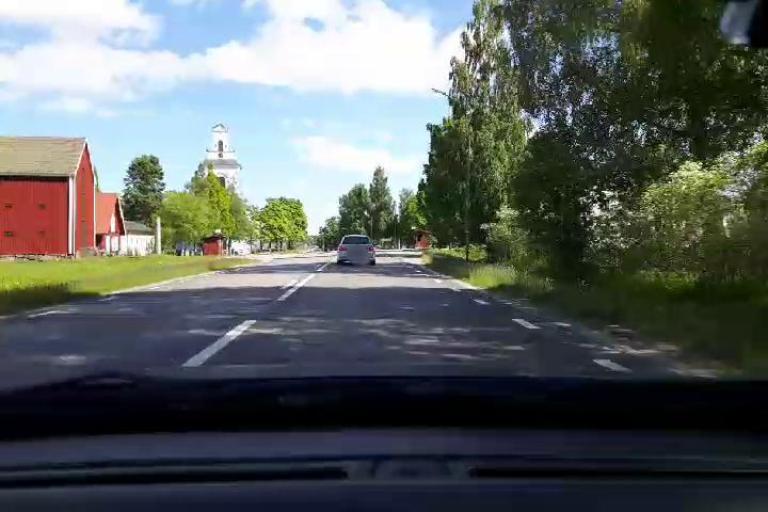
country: SE
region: Gaevleborg
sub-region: Hudiksvalls Kommun
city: Sorforsa
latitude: 61.7345
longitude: 16.9354
